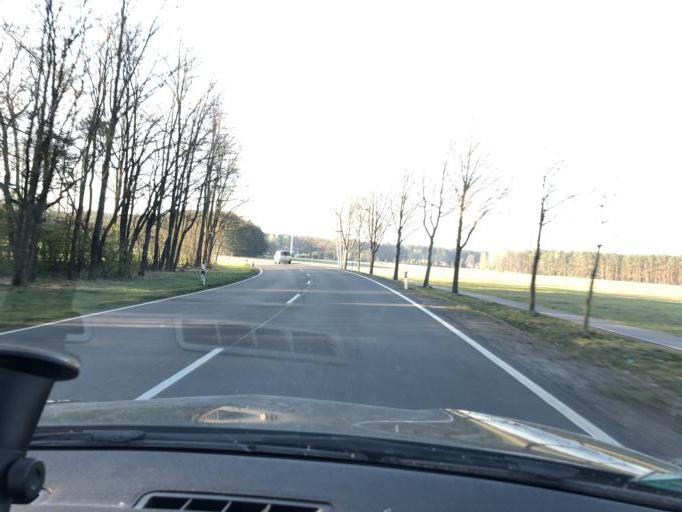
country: DE
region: Saxony
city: Weisskeissel
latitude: 51.4759
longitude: 14.7225
